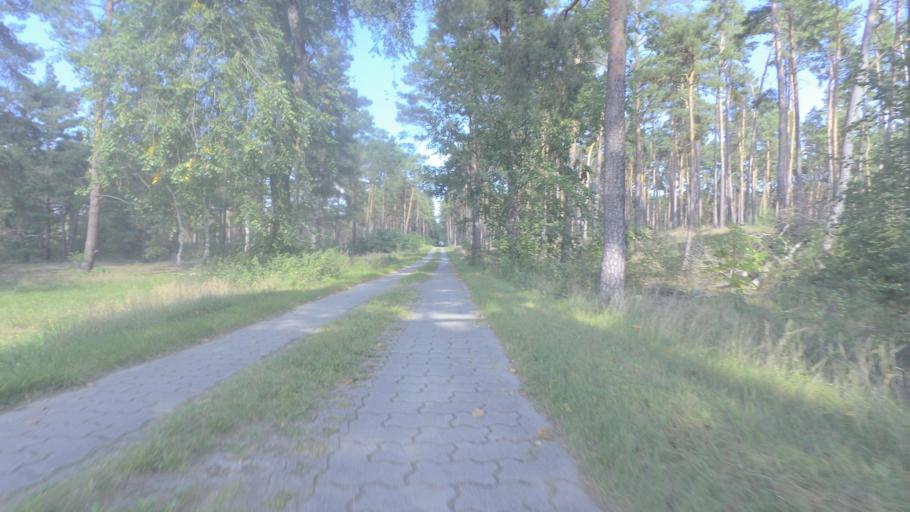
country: DE
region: Brandenburg
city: Munchehofe
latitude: 52.1863
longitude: 13.8731
